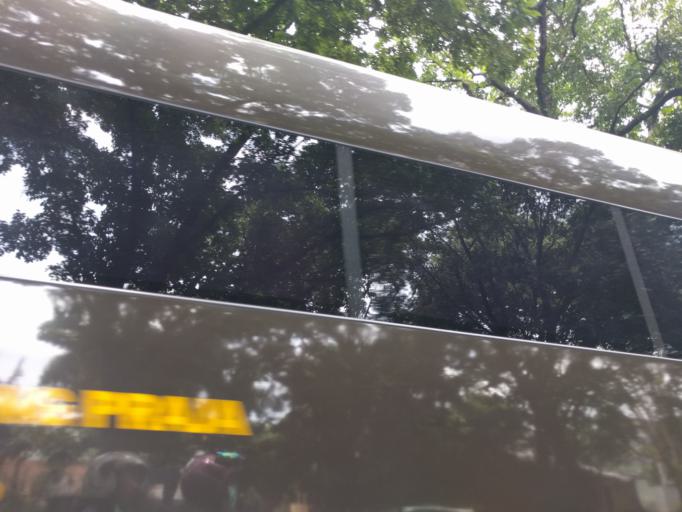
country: ID
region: West Java
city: Bogor
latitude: -6.5742
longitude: 106.8081
